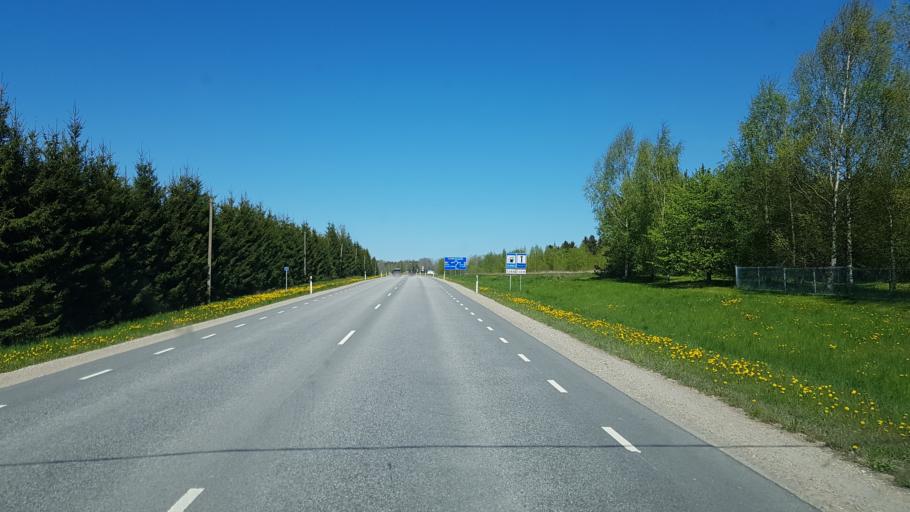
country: EE
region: Viljandimaa
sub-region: Viljandi linn
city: Viljandi
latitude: 58.3515
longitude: 25.5615
